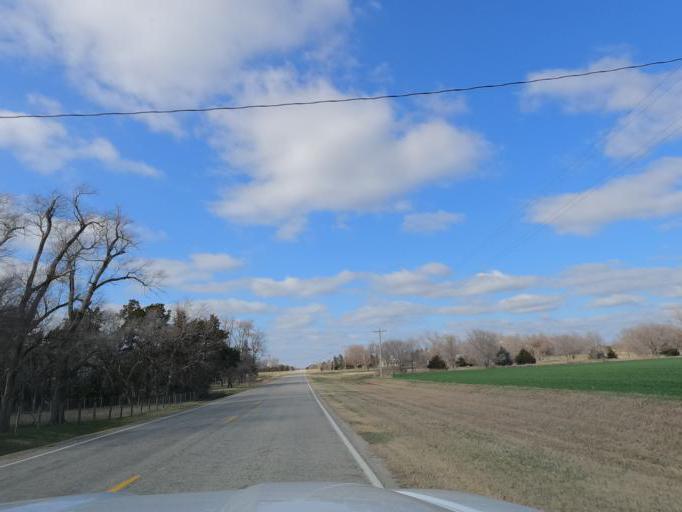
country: US
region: Kansas
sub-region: McPherson County
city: Inman
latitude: 38.2079
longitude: -97.8485
